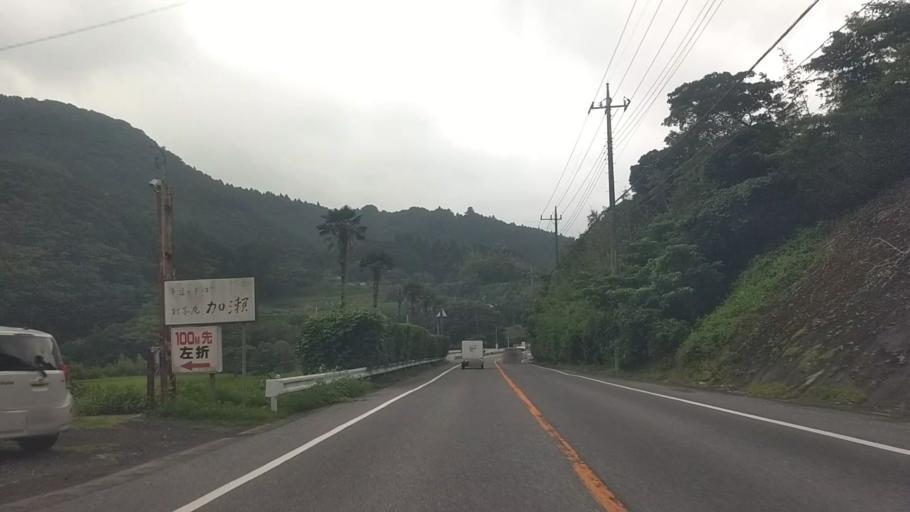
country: JP
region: Chiba
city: Kawaguchi
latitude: 35.1449
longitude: 140.0689
